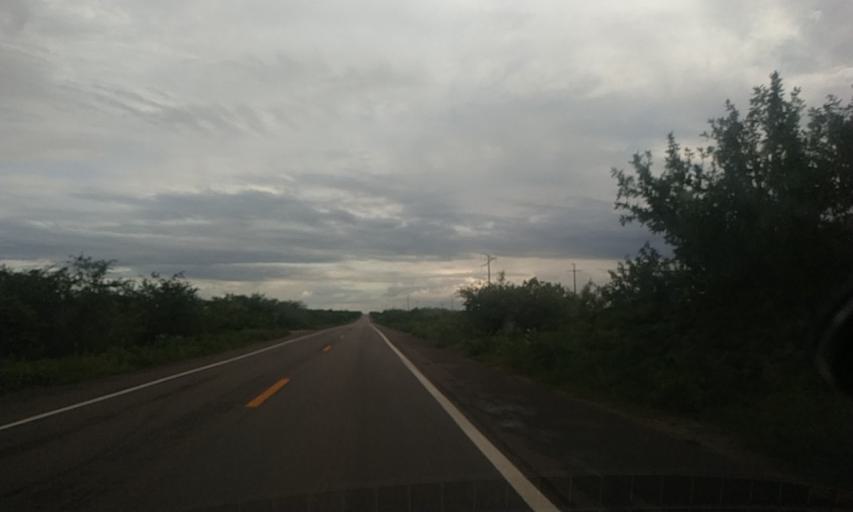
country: BR
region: Rio Grande do Norte
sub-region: Mossoro
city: Mossoro
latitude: -5.1389
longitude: -37.2122
